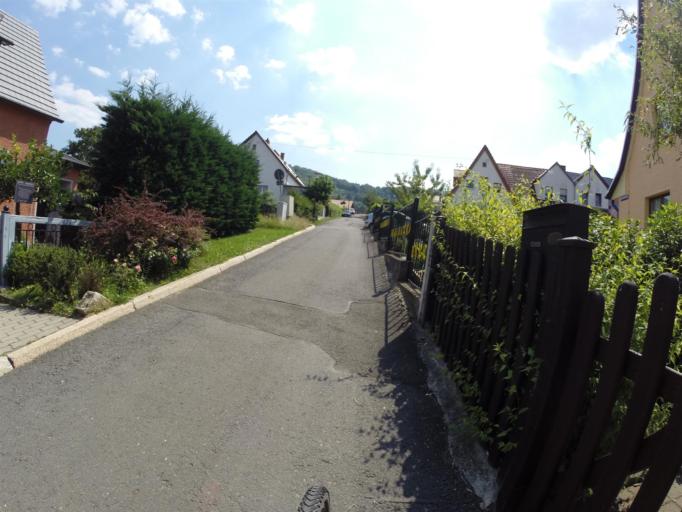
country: DE
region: Thuringia
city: Jena
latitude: 50.9315
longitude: 11.6142
